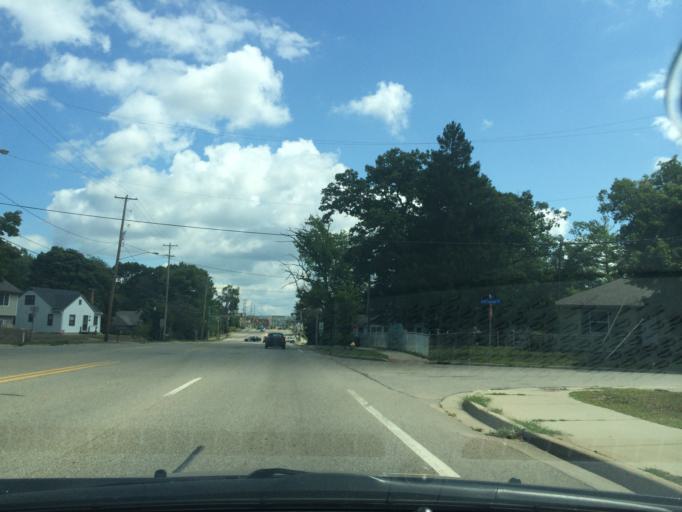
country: US
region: Michigan
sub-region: Kalamazoo County
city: Westwood
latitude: 42.2800
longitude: -85.6269
